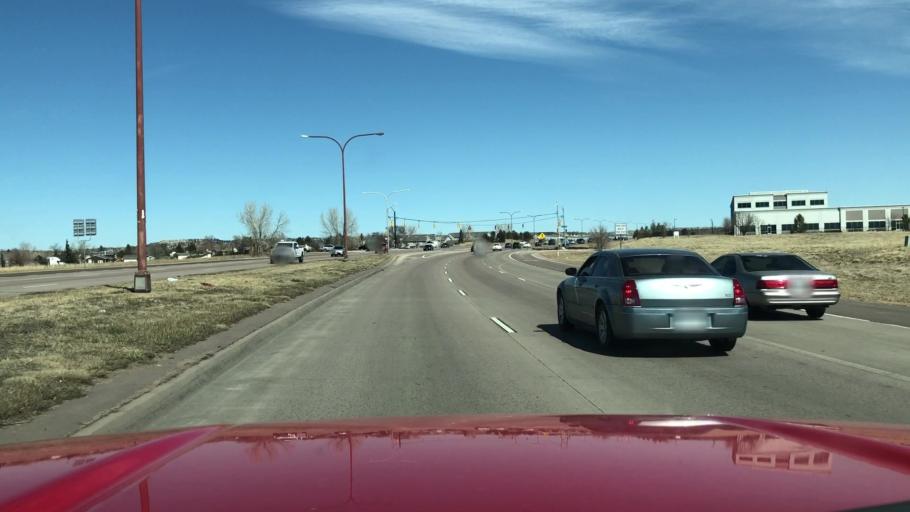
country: US
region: Colorado
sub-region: El Paso County
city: Cimarron Hills
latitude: 38.8145
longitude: -104.7300
